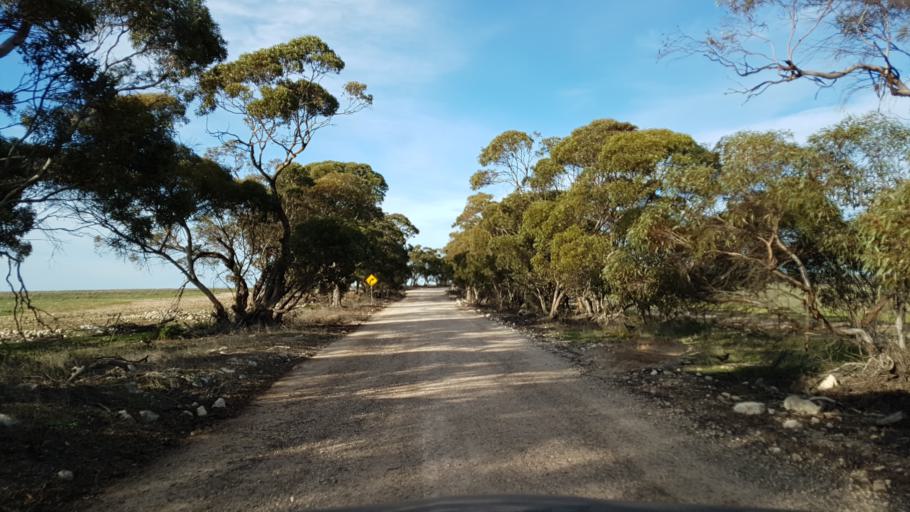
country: AU
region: South Australia
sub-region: Mid Murray
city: Mannum
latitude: -34.9759
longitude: 139.5762
